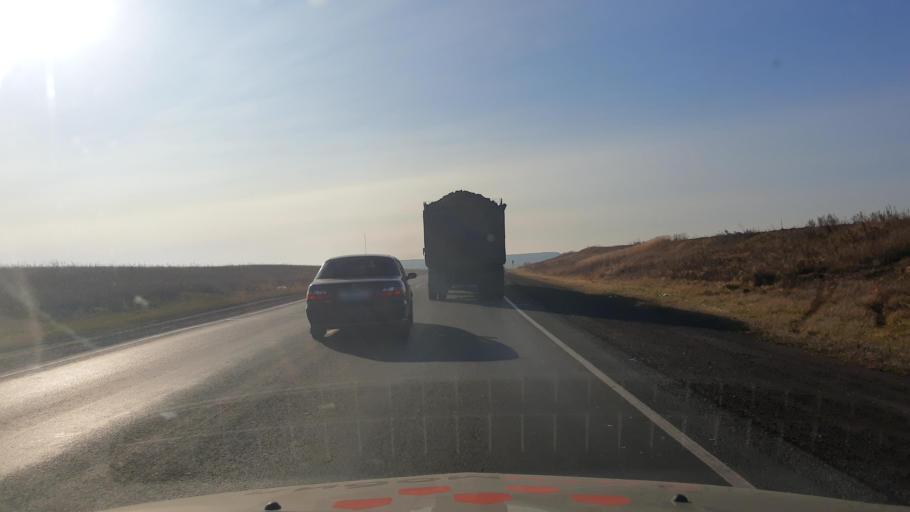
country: RU
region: Bashkortostan
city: Avdon
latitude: 54.7137
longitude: 55.7764
